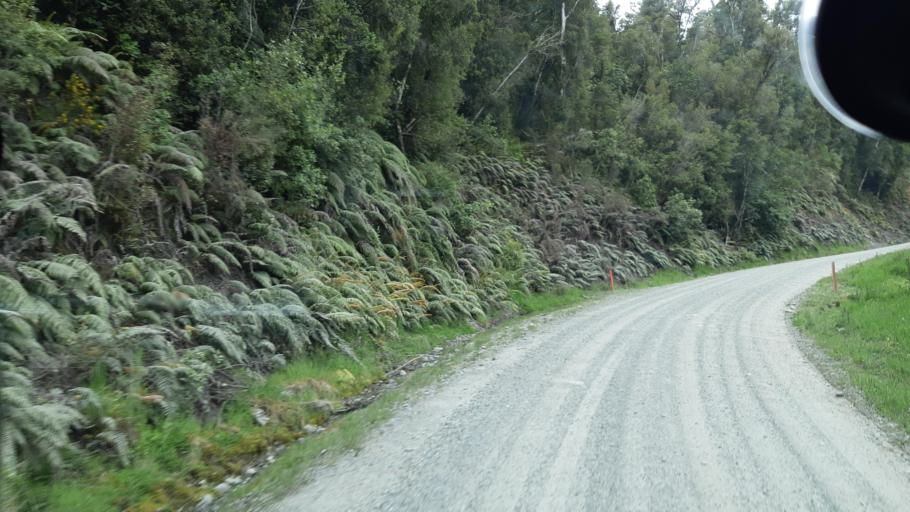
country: NZ
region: West Coast
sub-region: Grey District
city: Greymouth
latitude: -42.6456
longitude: 171.3501
